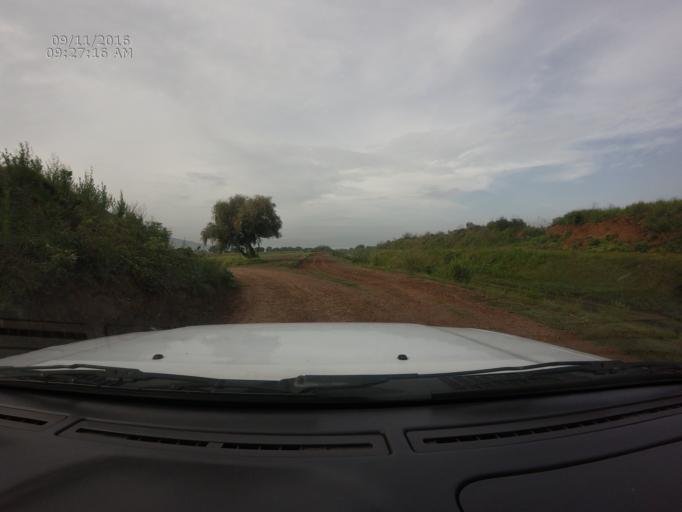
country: MX
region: Michoacan
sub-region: Morelia
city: La Mintzita (Piedra Dura)
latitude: 19.5905
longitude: -101.2911
